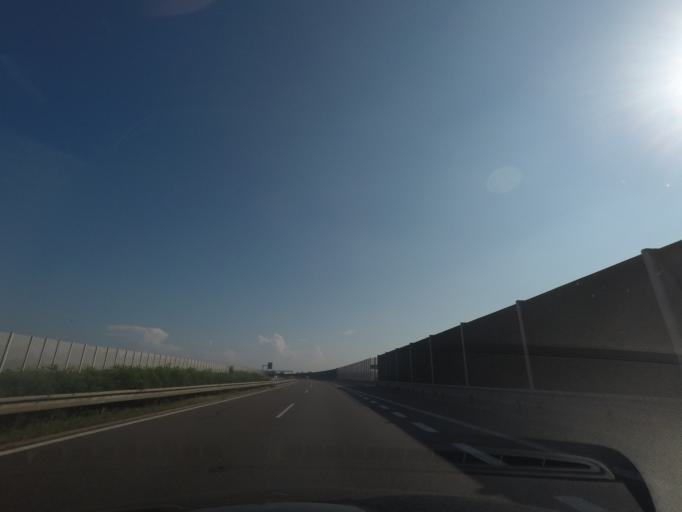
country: PL
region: Silesian Voivodeship
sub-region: Powiat raciborski
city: Chalupki
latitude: 49.8996
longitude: 18.3042
